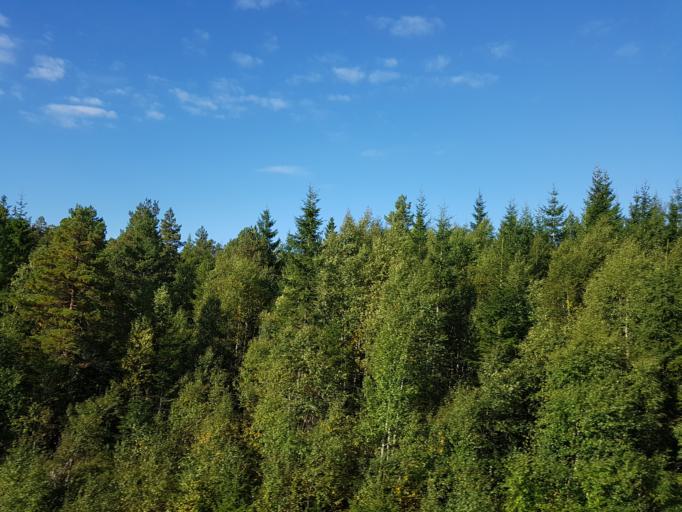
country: NO
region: Sor-Trondelag
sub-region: Trondheim
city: Trondheim
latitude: 63.6121
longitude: 10.2376
